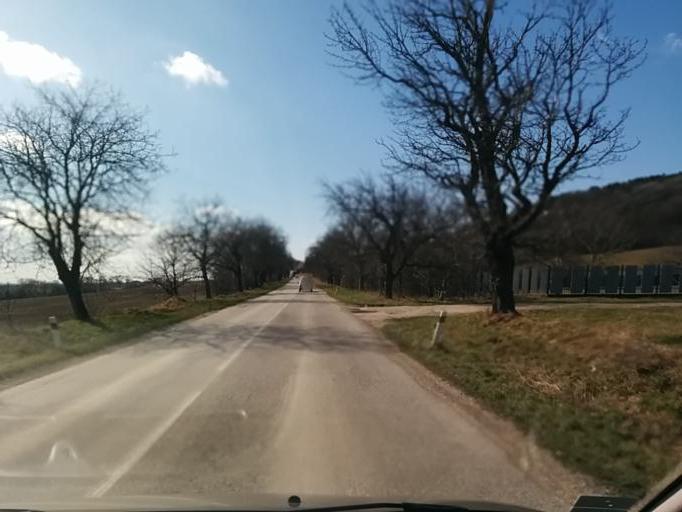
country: SK
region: Trenciansky
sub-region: Okres Nove Mesto nad Vahom
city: Nove Mesto nad Vahom
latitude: 48.7401
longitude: 17.8172
